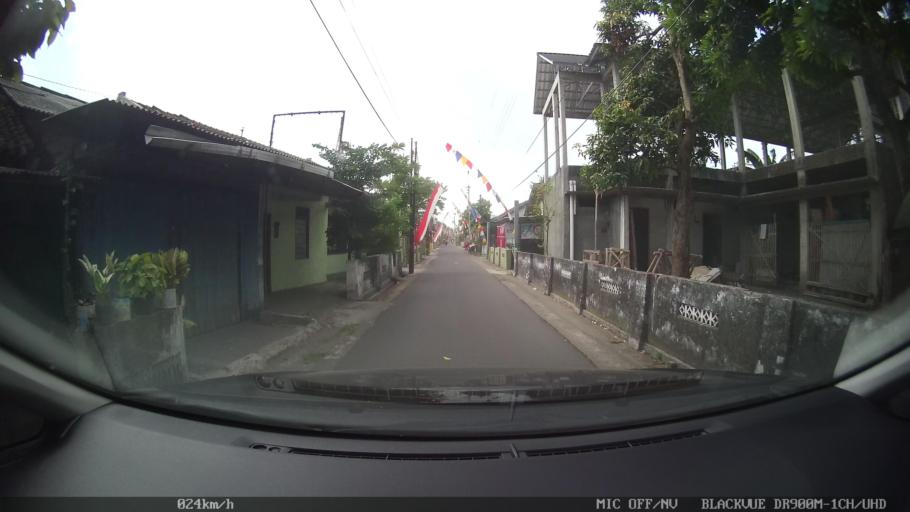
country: ID
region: Daerah Istimewa Yogyakarta
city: Gamping Lor
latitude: -7.8039
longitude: 110.3379
